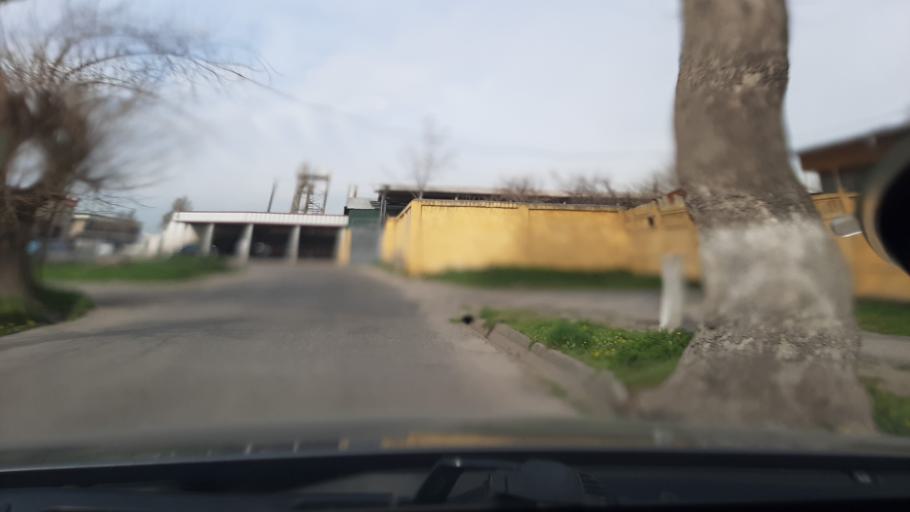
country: TJ
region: Dushanbe
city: Dushanbe
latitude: 38.5705
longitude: 68.7612
